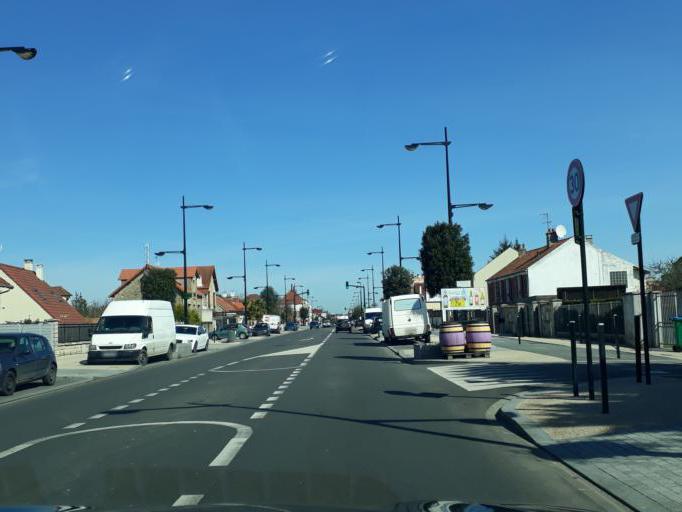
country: FR
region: Ile-de-France
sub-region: Departement de l'Essonne
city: Saintry-sur-Seine
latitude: 48.5806
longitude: 2.4763
